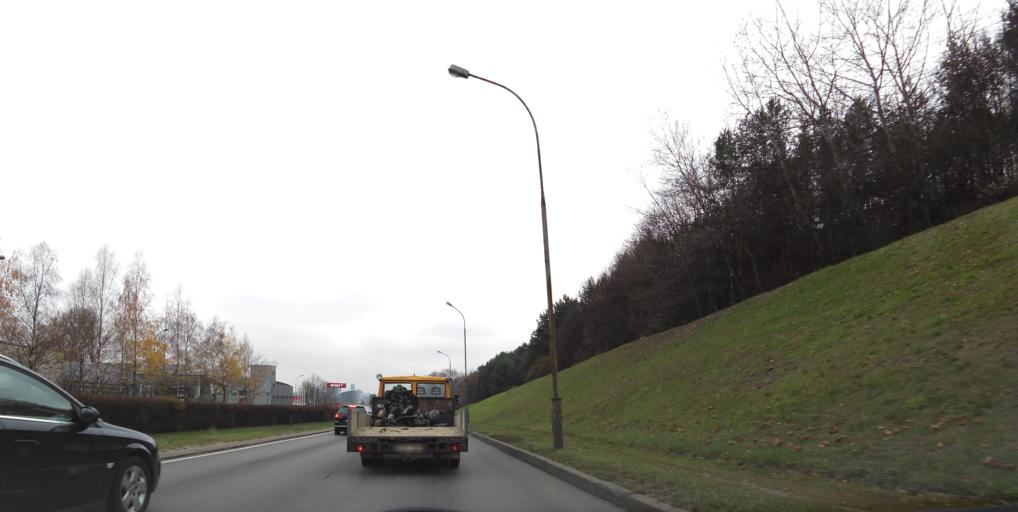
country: LT
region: Vilnius County
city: Seskine
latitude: 54.7085
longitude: 25.2681
